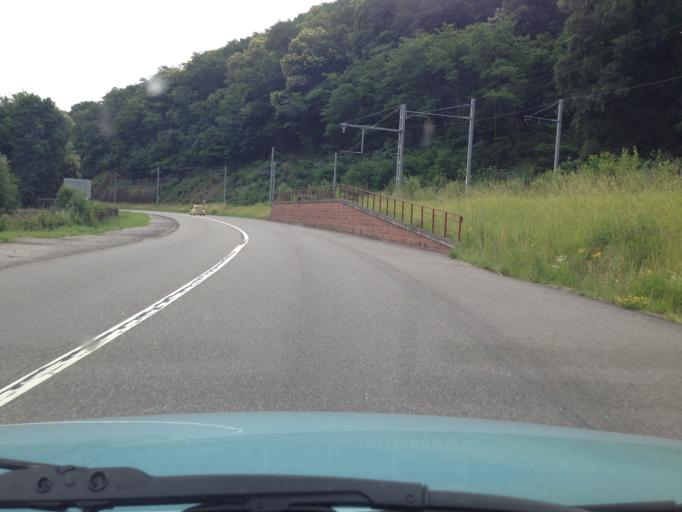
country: FR
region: Alsace
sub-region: Departement du Haut-Rhin
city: Thann
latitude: 47.8142
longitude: 7.0884
